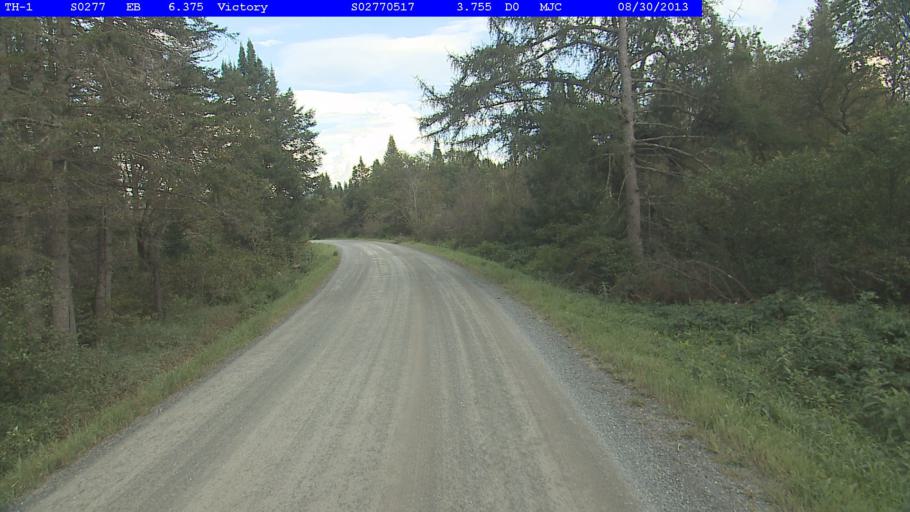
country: US
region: Vermont
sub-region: Caledonia County
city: Lyndonville
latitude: 44.5303
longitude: -71.8036
